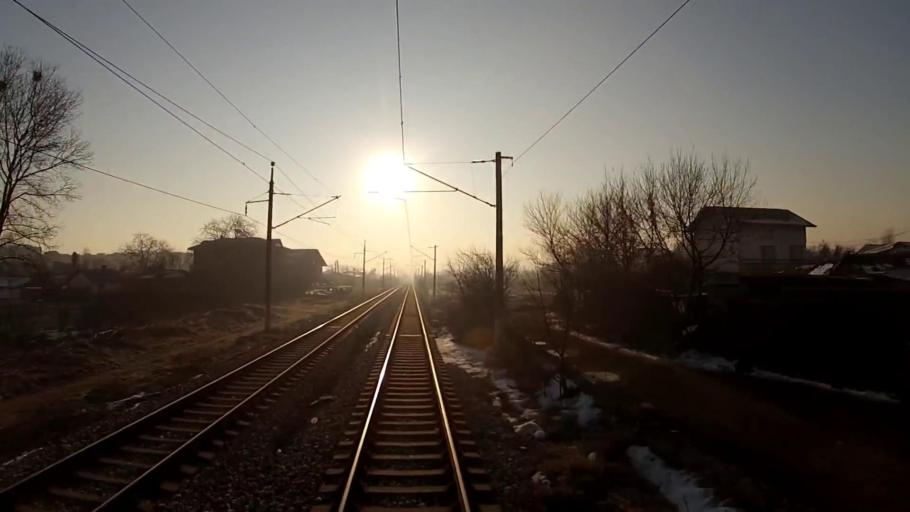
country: BG
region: Sofia-Capital
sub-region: Stolichna Obshtina
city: Sofia
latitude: 42.7337
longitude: 23.2694
